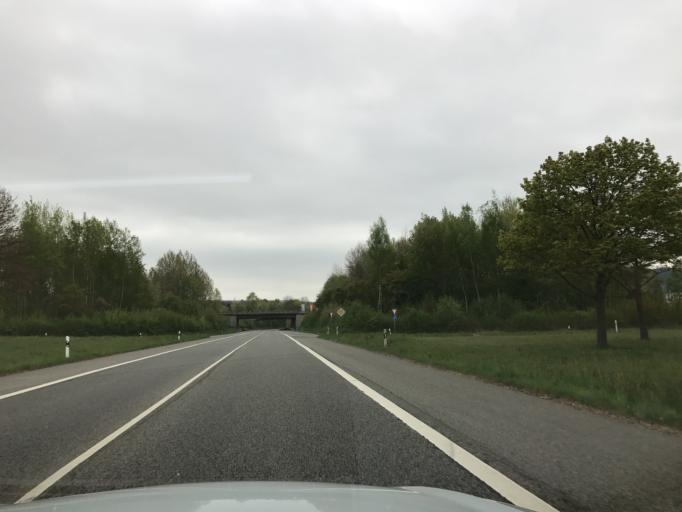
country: DE
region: Rheinland-Pfalz
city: Ockfen
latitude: 49.6087
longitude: 6.5672
